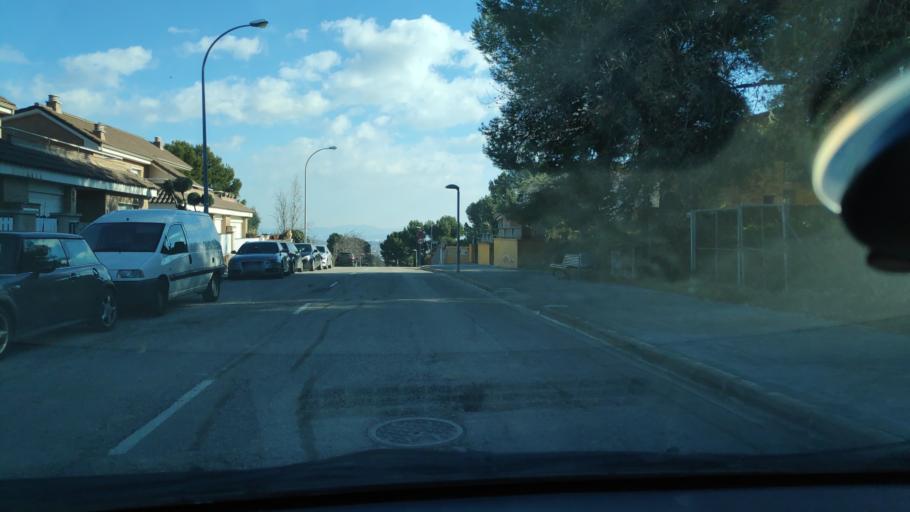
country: ES
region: Catalonia
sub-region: Provincia de Barcelona
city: Sant Quirze del Valles
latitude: 41.5233
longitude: 2.0725
